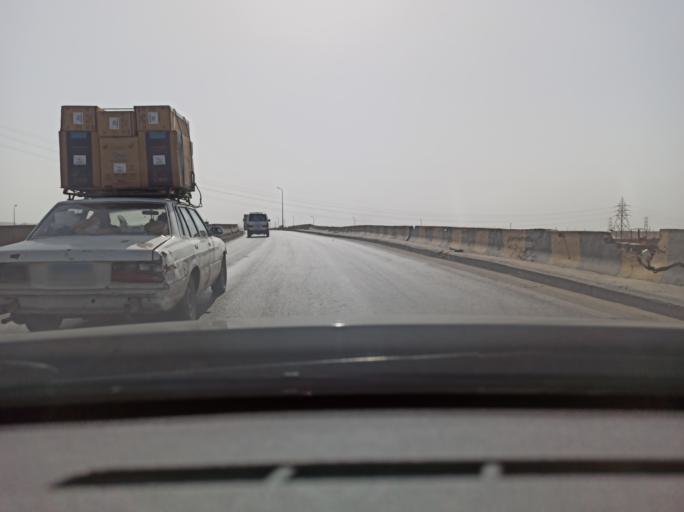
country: EG
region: Muhafazat al Qahirah
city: Halwan
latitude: 29.7900
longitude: 31.3459
